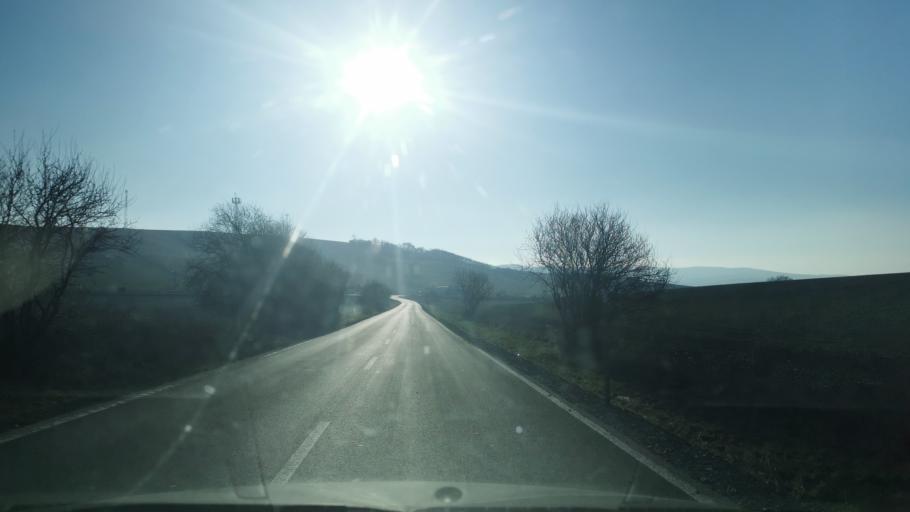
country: SK
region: Trnavsky
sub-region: Okres Senica
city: Senica
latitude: 48.7479
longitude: 17.3458
